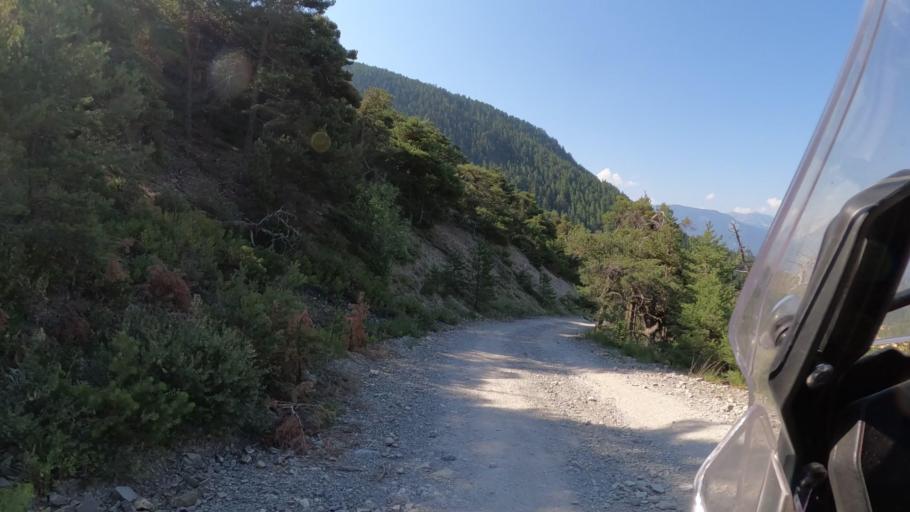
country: FR
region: Provence-Alpes-Cote d'Azur
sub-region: Departement des Hautes-Alpes
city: Embrun
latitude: 44.5855
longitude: 6.5521
